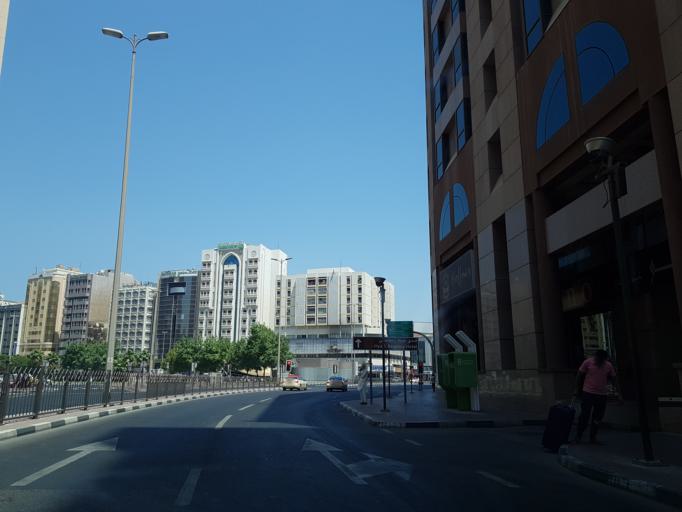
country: AE
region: Ash Shariqah
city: Sharjah
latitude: 25.2680
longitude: 55.3082
